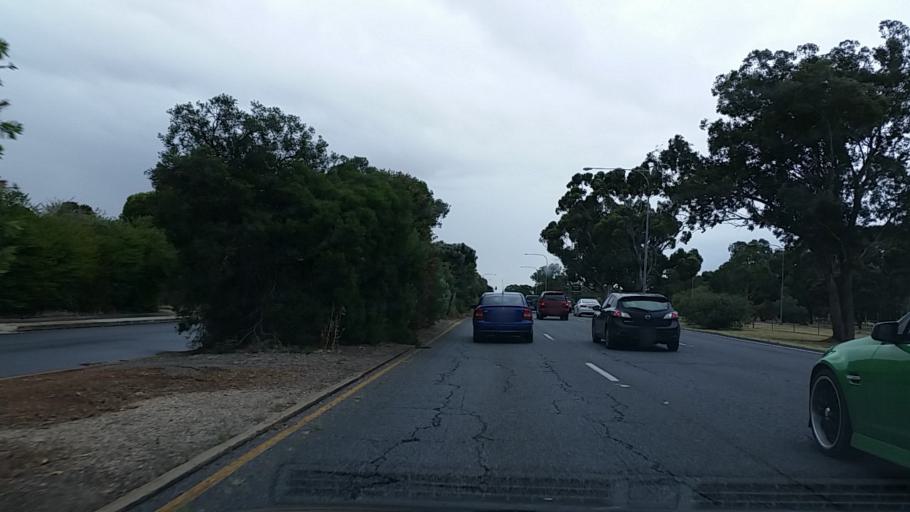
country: AU
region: South Australia
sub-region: Salisbury
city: Elizabeth
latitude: -34.7021
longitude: 138.6815
